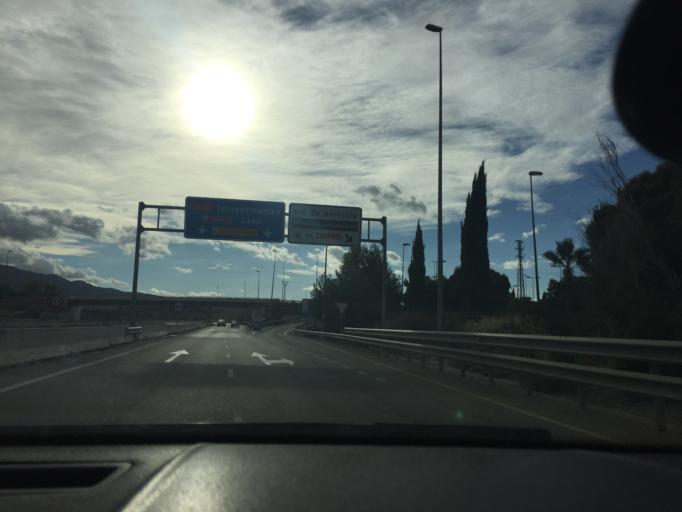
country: ES
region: Andalusia
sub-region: Provincia de Jaen
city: Jaen
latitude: 37.8161
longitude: -3.7697
